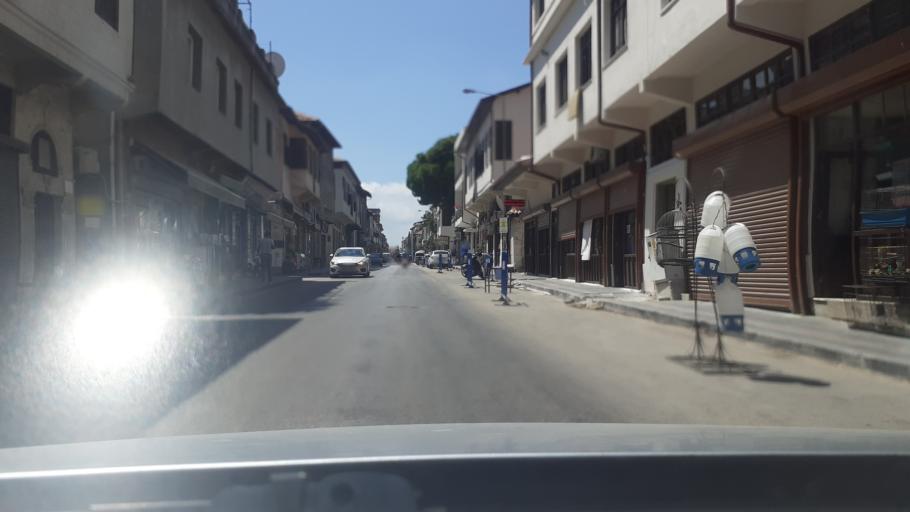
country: TR
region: Hatay
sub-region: Antakya Ilcesi
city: Antakya
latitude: 36.2010
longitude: 36.1652
